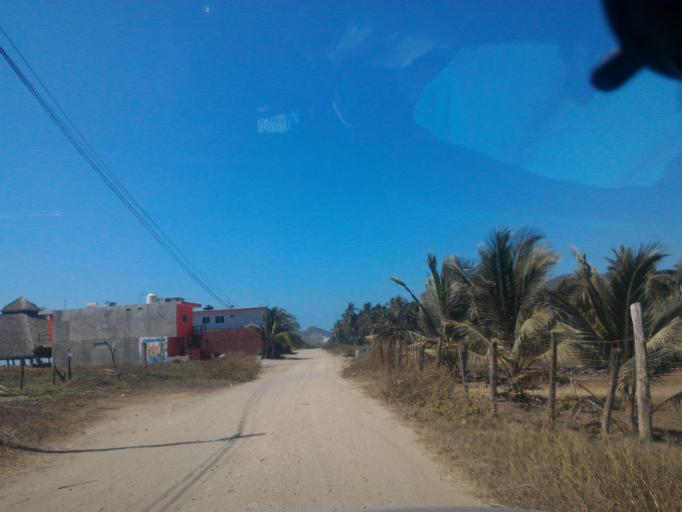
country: MX
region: Michoacan
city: Coahuayana Viejo
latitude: 18.5844
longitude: -103.6761
